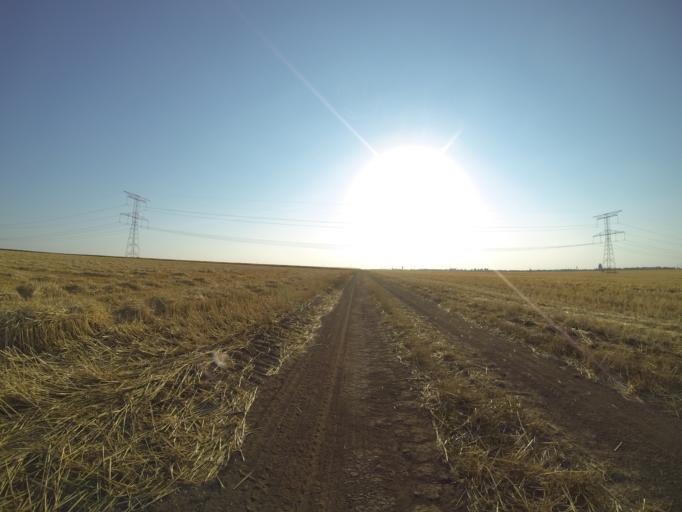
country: RO
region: Dolj
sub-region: Comuna Giurgita
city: Giurgita
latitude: 44.0289
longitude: 23.6657
